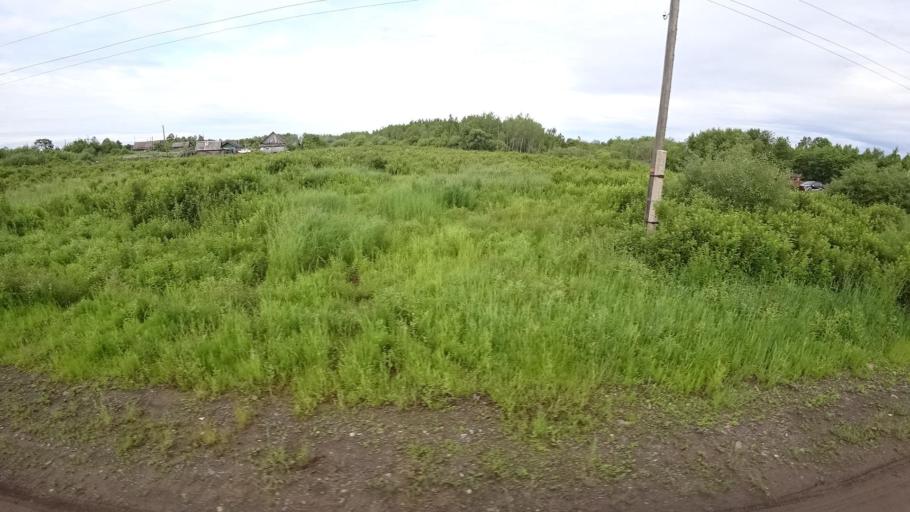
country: RU
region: Khabarovsk Krai
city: Amursk
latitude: 49.8851
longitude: 136.1282
